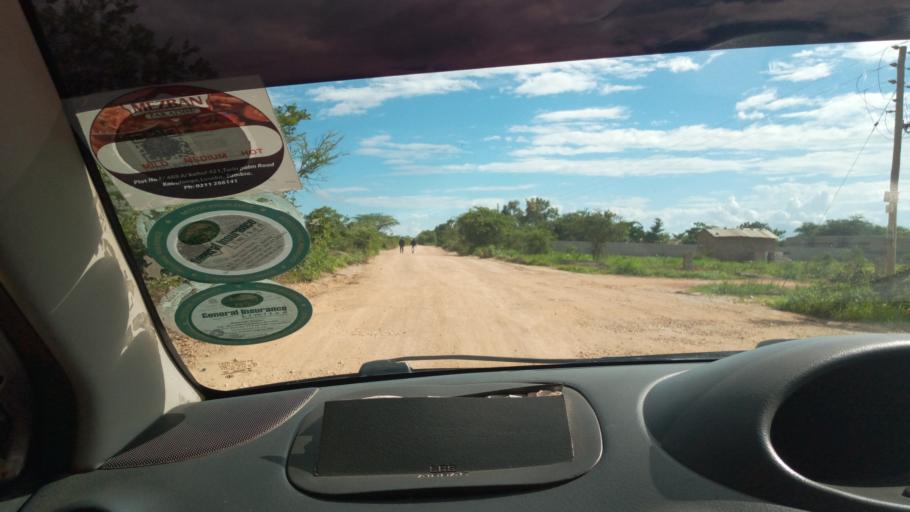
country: ZM
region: Lusaka
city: Lusaka
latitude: -15.5213
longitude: 28.3420
